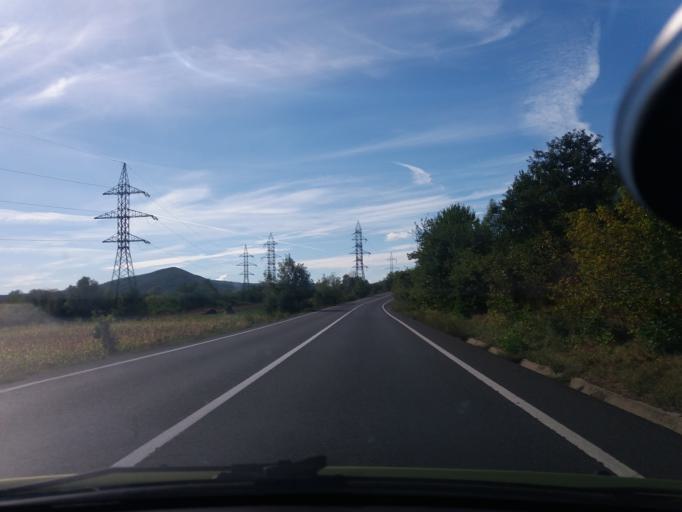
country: RO
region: Hunedoara
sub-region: Comuna Dobra
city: Dobra
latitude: 45.9393
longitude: 22.5299
